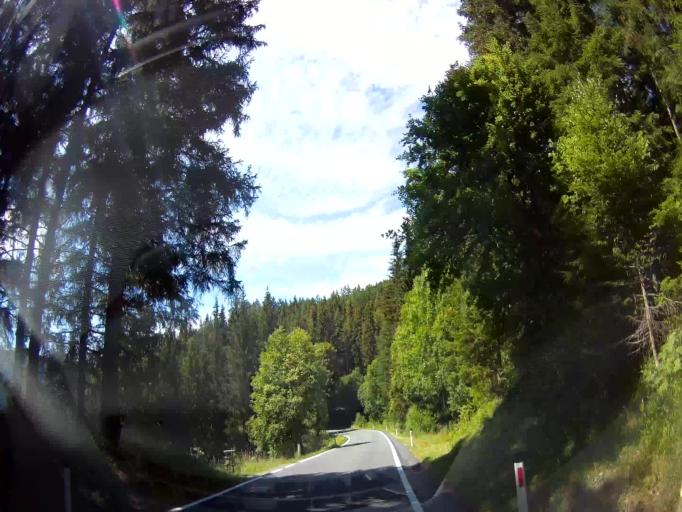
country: AT
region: Carinthia
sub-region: Politischer Bezirk Sankt Veit an der Glan
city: Glodnitz
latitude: 46.9171
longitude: 14.0660
